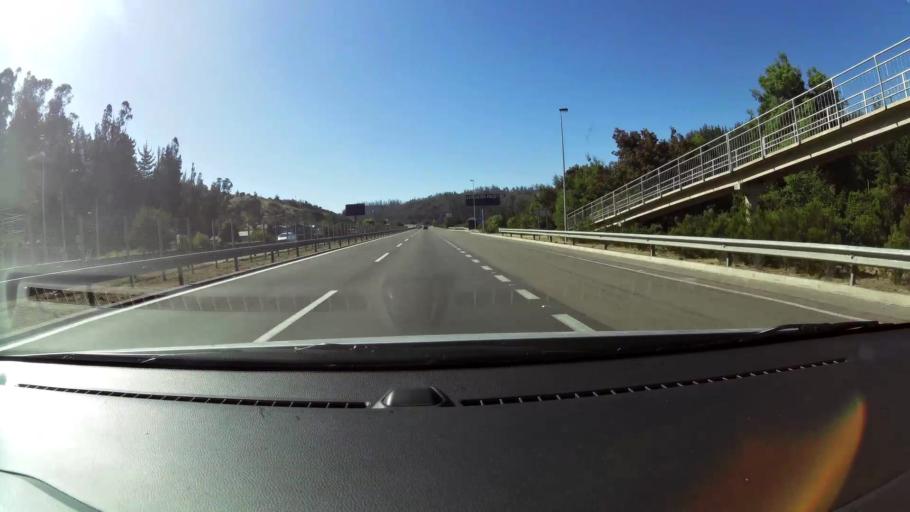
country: CL
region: Valparaiso
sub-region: Provincia de Marga Marga
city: Quilpue
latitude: -33.2204
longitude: -71.4712
